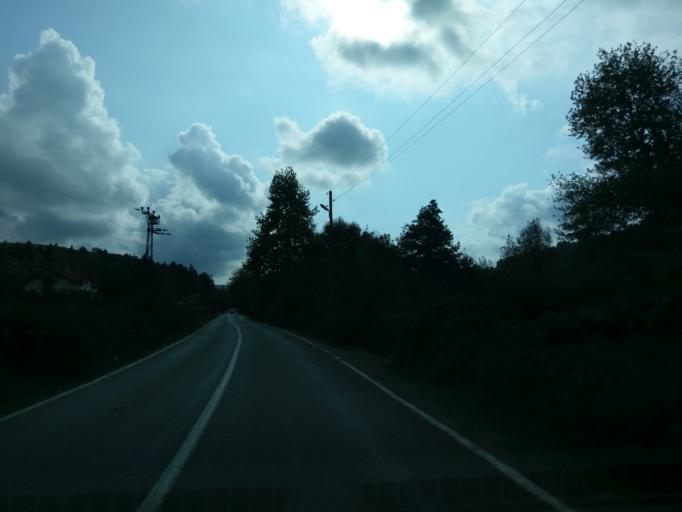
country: TR
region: Sinop
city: Helaldi
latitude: 41.9017
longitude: 34.4544
